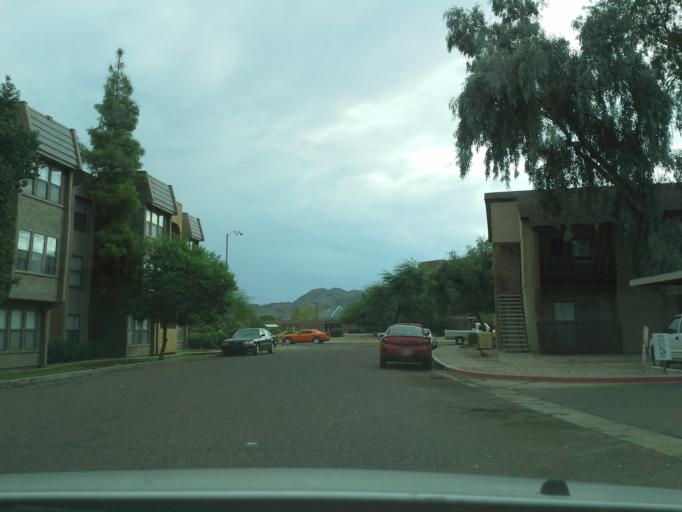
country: US
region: Arizona
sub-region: Maricopa County
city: Paradise Valley
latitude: 33.5971
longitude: -111.9845
